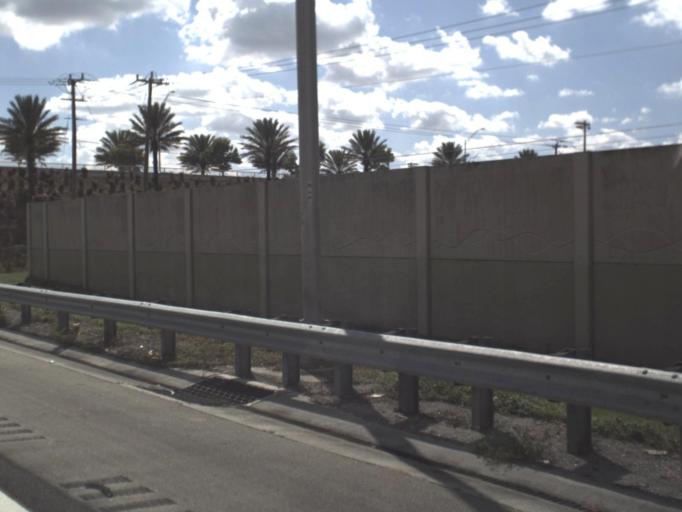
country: US
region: Florida
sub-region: Broward County
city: Broadview Park
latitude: 26.1070
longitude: -80.2185
